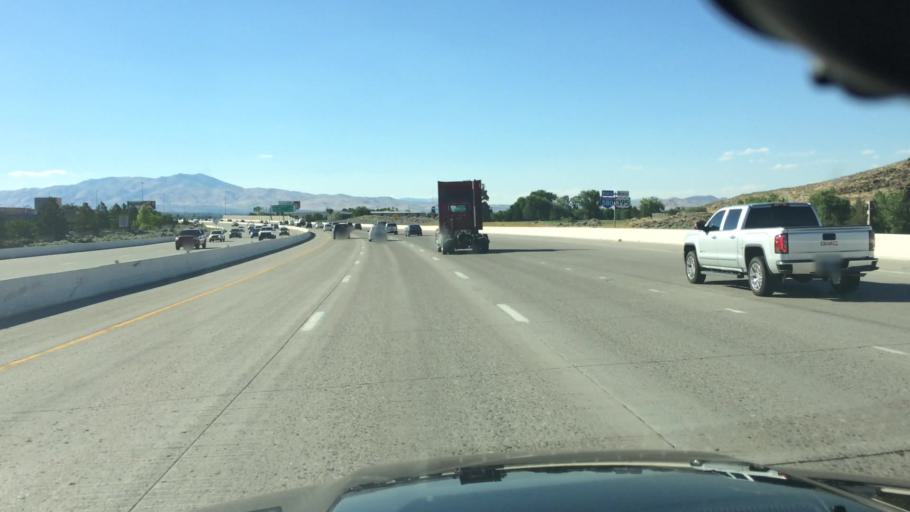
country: US
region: Nevada
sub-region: Washoe County
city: Sparks
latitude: 39.4434
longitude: -119.7674
